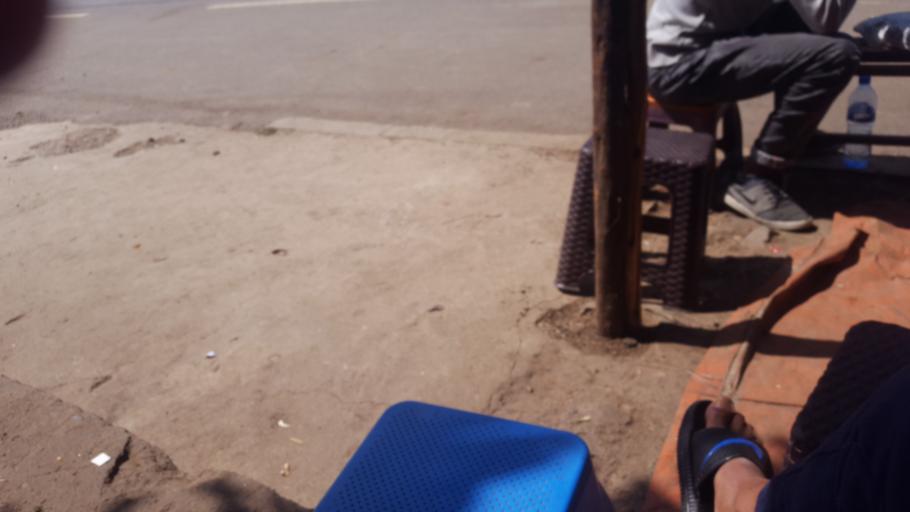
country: ET
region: Adis Abeba
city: Addis Ababa
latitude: 9.0054
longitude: 38.7065
